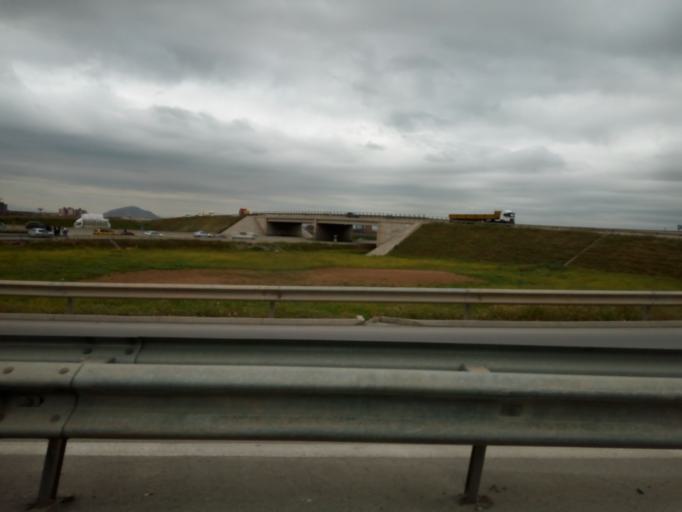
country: DZ
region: Setif
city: El Eulma
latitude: 36.1779
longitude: 5.6759
